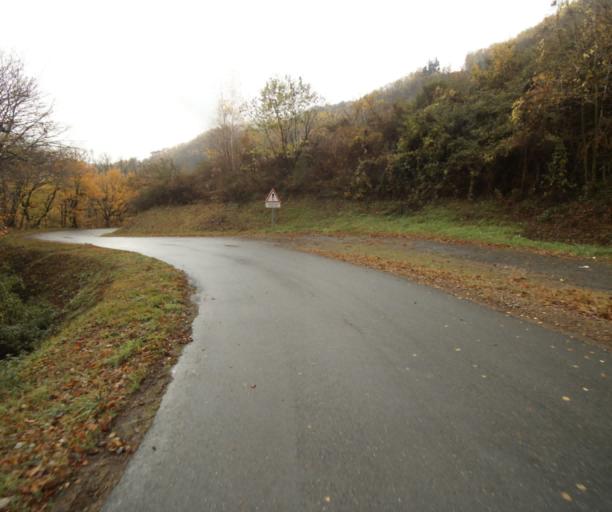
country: FR
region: Limousin
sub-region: Departement de la Correze
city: Cornil
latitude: 45.1965
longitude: 1.6520
